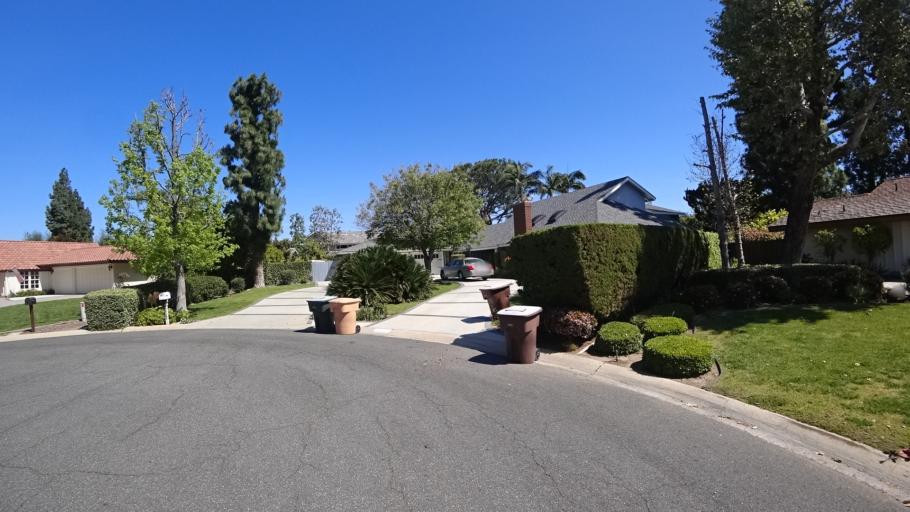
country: US
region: California
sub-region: Orange County
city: Villa Park
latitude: 33.8158
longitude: -117.8029
